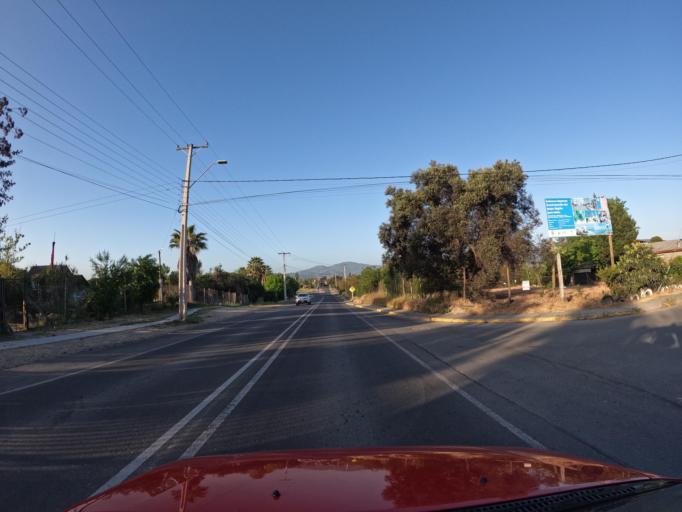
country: CL
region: O'Higgins
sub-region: Provincia de Colchagua
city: Santa Cruz
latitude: -34.3166
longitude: -71.3861
